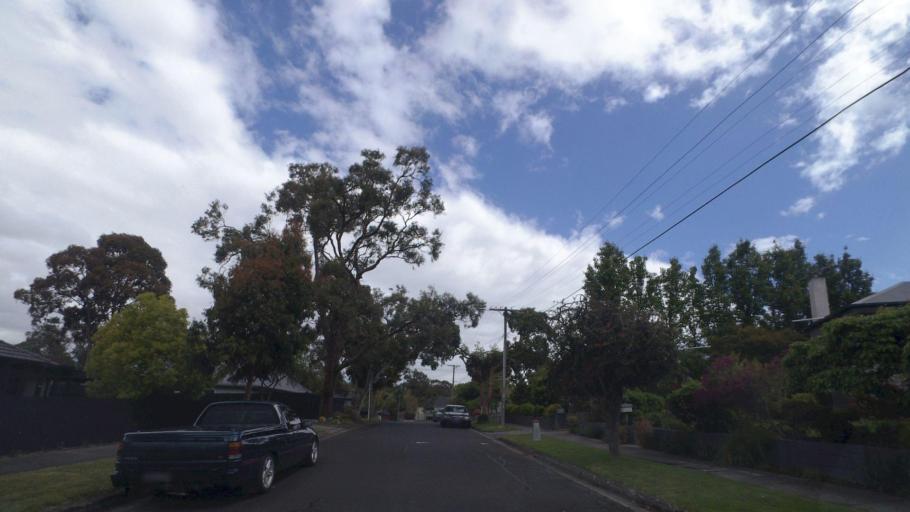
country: AU
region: Victoria
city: Mitcham
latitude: -37.8252
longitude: 145.1979
